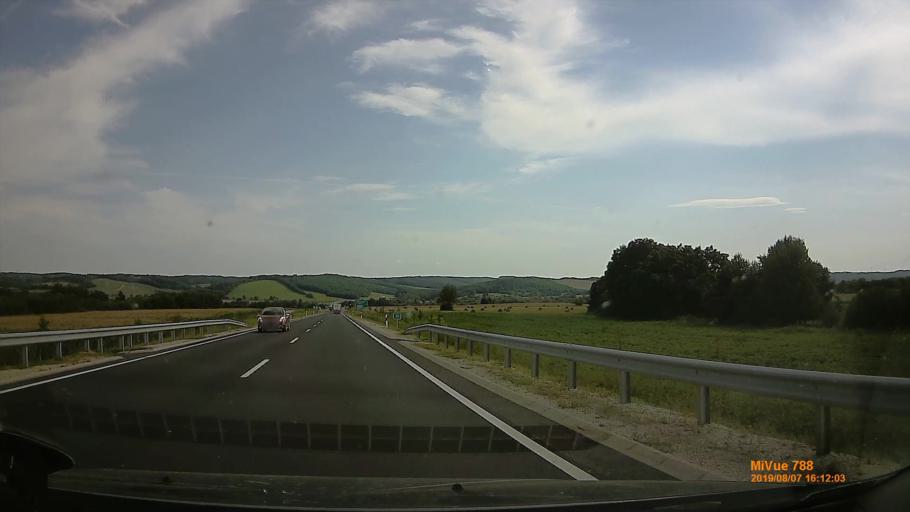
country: HU
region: Zala
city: Zalalovo
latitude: 46.8616
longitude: 16.6263
